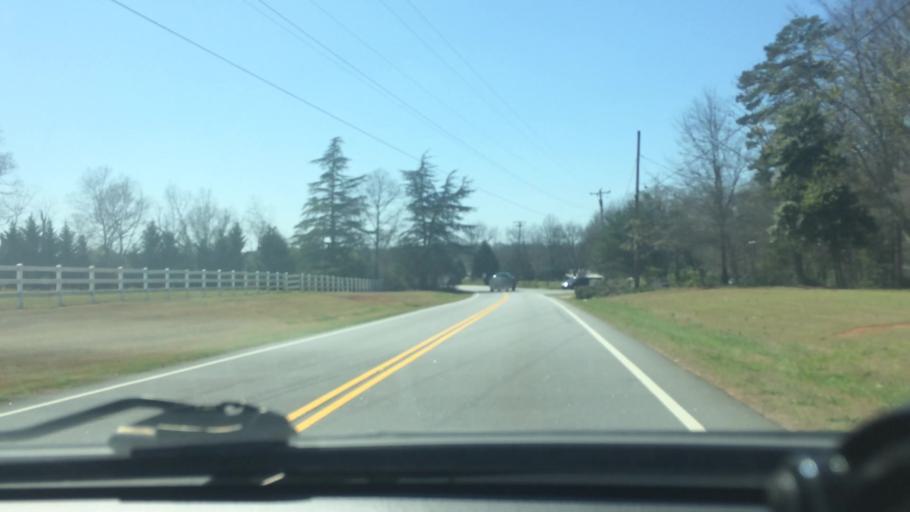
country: US
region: South Carolina
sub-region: Anderson County
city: Powdersville
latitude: 34.7885
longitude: -82.4978
